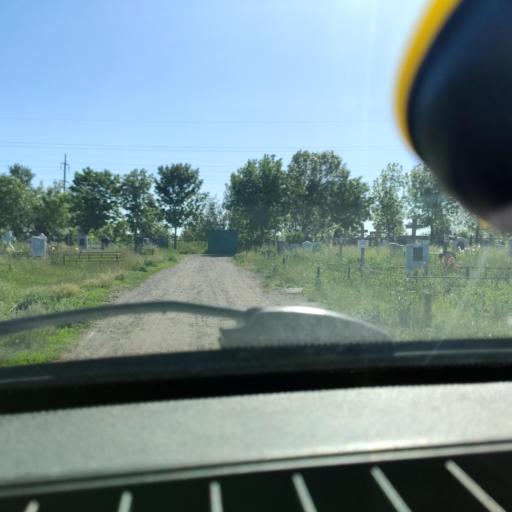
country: RU
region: Samara
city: Tol'yatti
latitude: 53.5722
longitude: 49.4295
